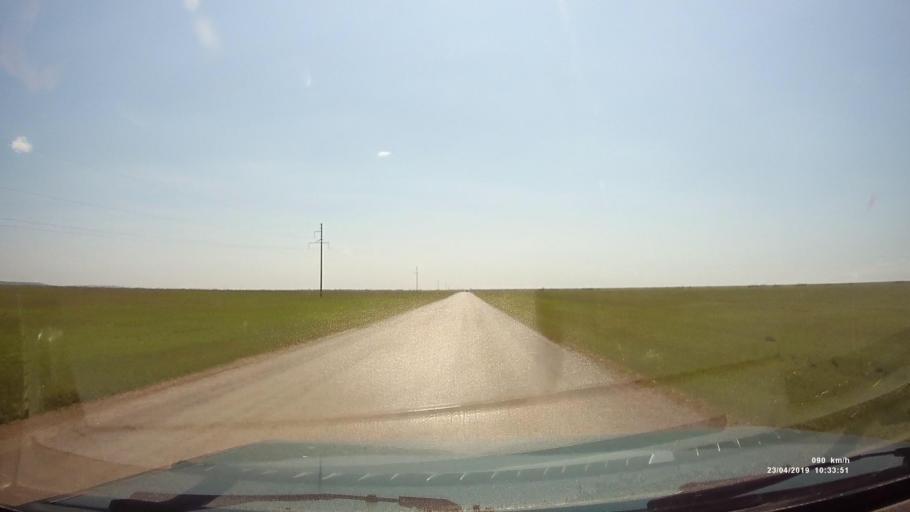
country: RU
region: Kalmykiya
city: Yashalta
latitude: 46.5697
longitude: 42.6026
